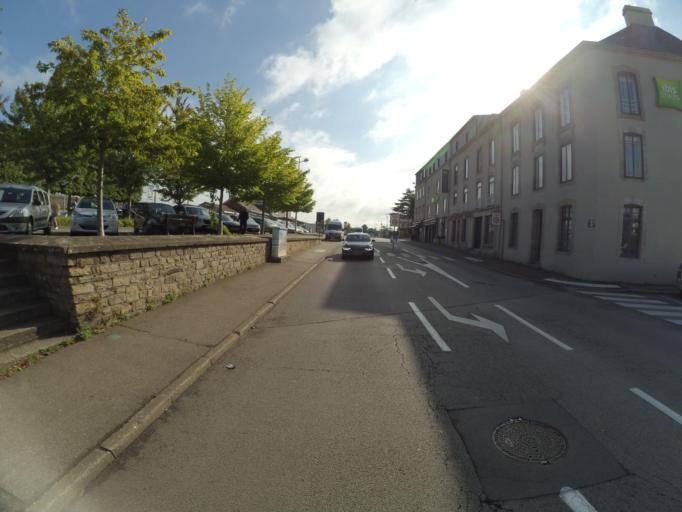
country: FR
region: Brittany
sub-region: Departement du Morbihan
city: Vannes
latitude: 47.6646
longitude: -2.7535
